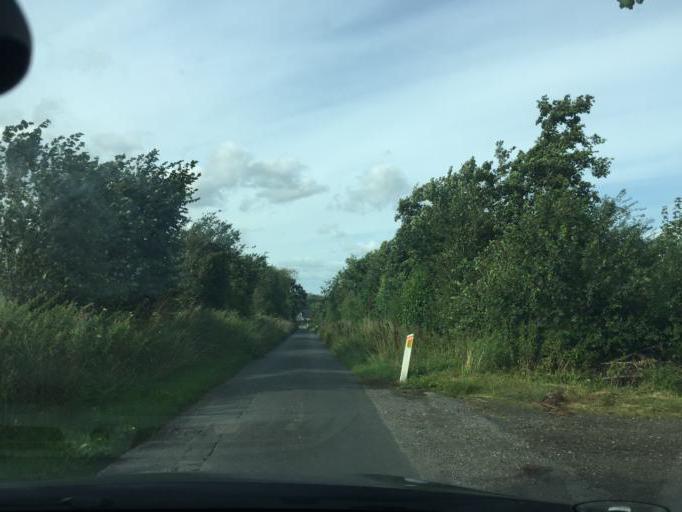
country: DK
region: South Denmark
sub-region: Faaborg-Midtfyn Kommune
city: Arslev
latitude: 55.3473
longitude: 10.5132
